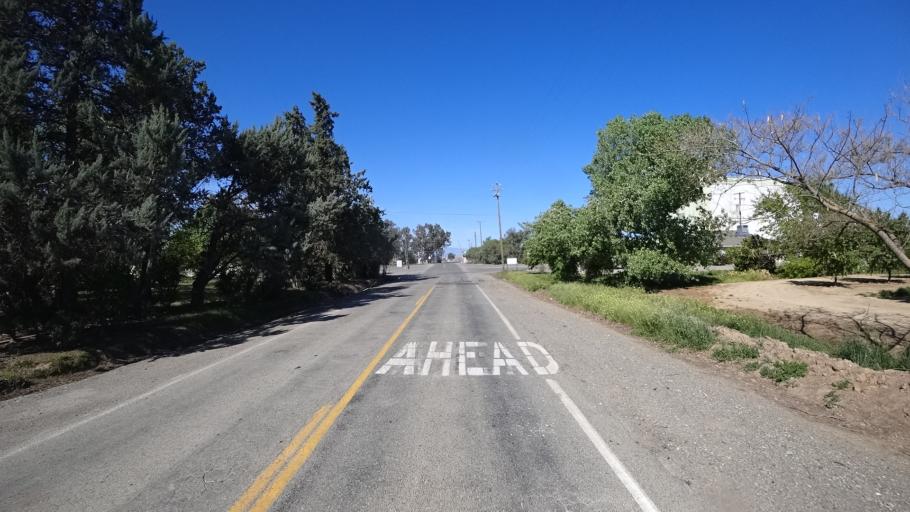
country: US
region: California
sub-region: Glenn County
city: Willows
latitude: 39.6241
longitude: -122.1927
